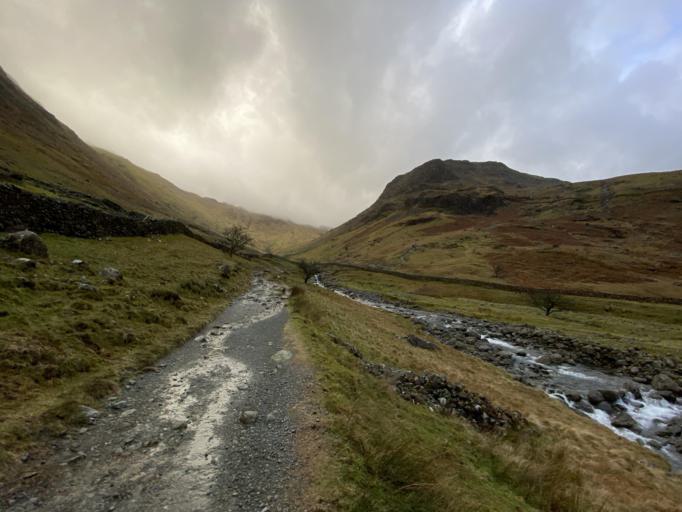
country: GB
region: England
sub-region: Cumbria
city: Keswick
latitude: 54.4889
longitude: -3.1828
